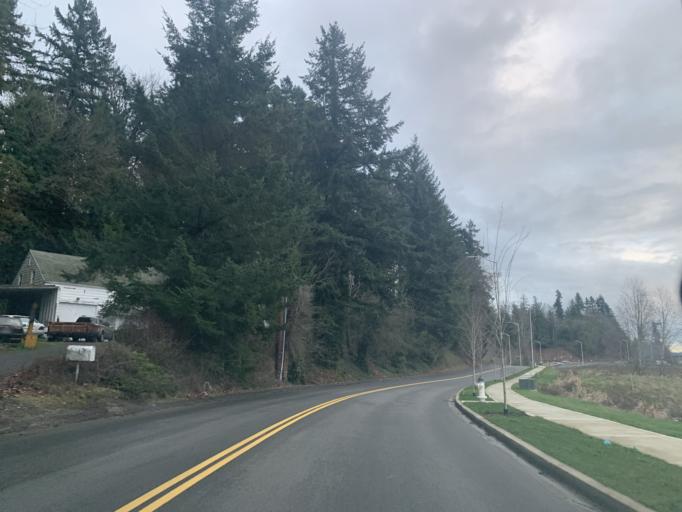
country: US
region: Washington
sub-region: Pierce County
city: Milton
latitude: 47.2372
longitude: -122.3253
